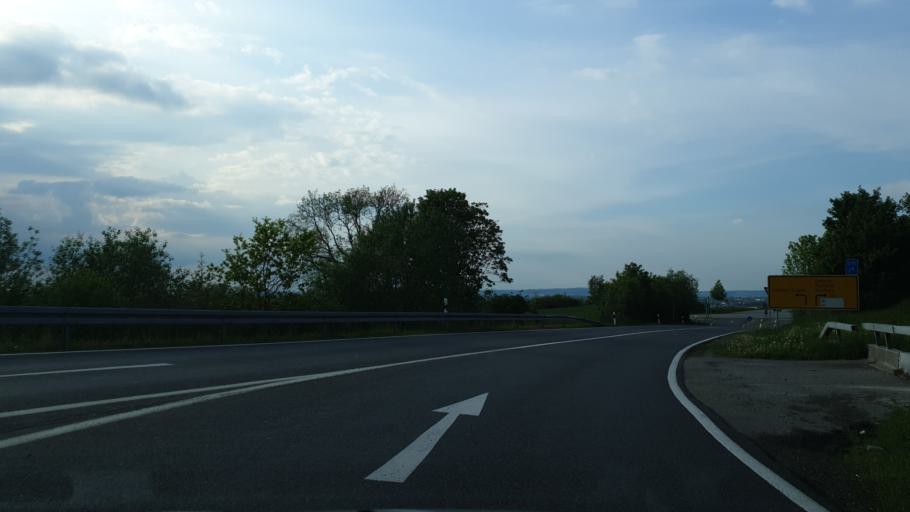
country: DE
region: Saxony
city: Stollberg
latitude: 50.7030
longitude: 12.7495
